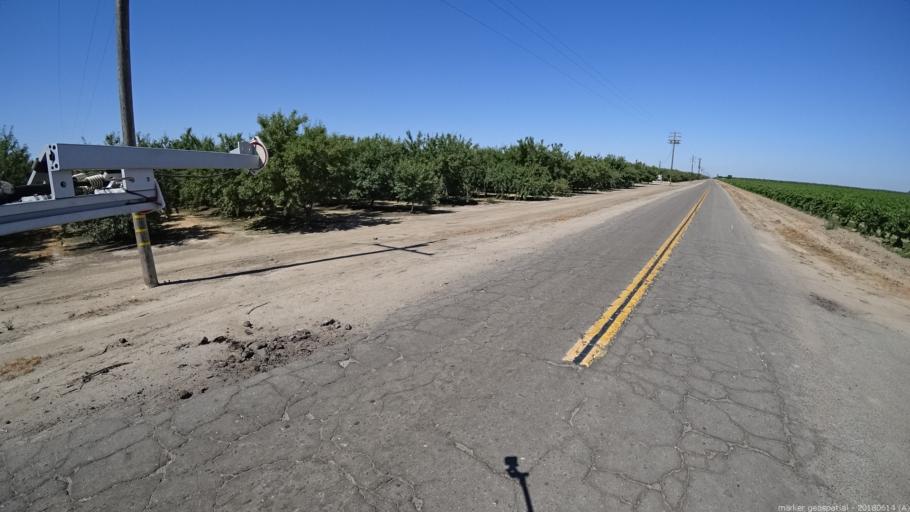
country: US
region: California
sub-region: Madera County
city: Fairmead
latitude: 36.9382
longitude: -120.2108
